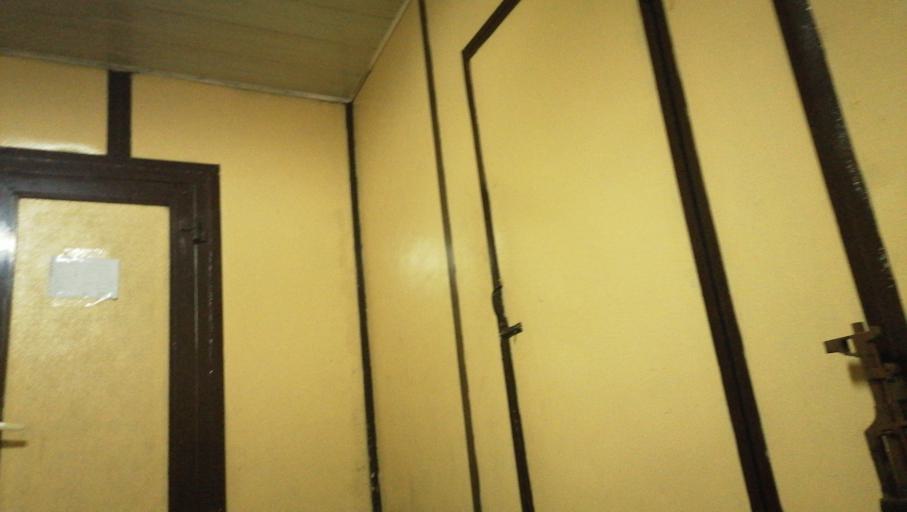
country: NG
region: Rivers
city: Bori
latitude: 4.5737
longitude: 7.2535
